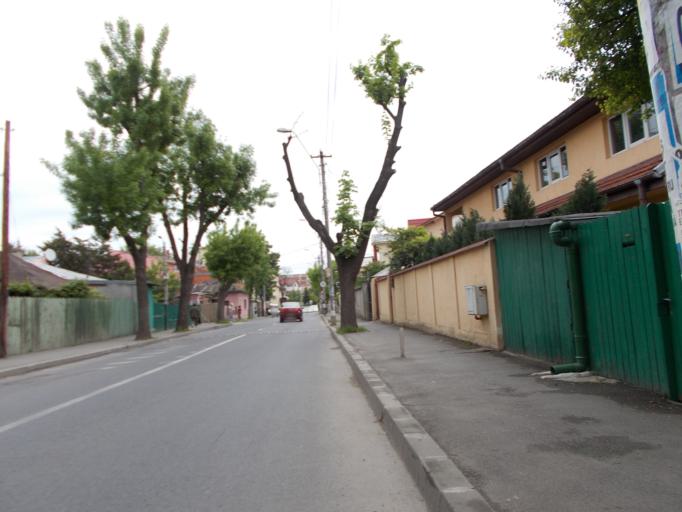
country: RO
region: Bucuresti
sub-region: Municipiul Bucuresti
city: Bucuresti
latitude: 44.3943
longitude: 26.1022
